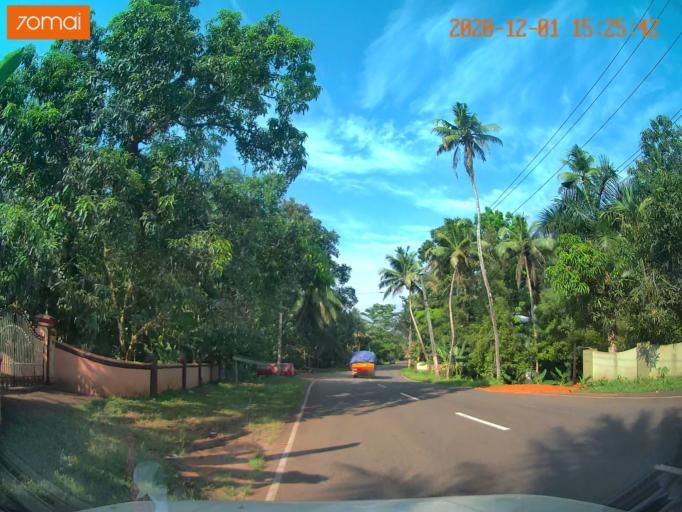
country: IN
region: Kerala
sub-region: Ernakulam
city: Muvattupuzha
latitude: 9.9576
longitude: 76.5613
